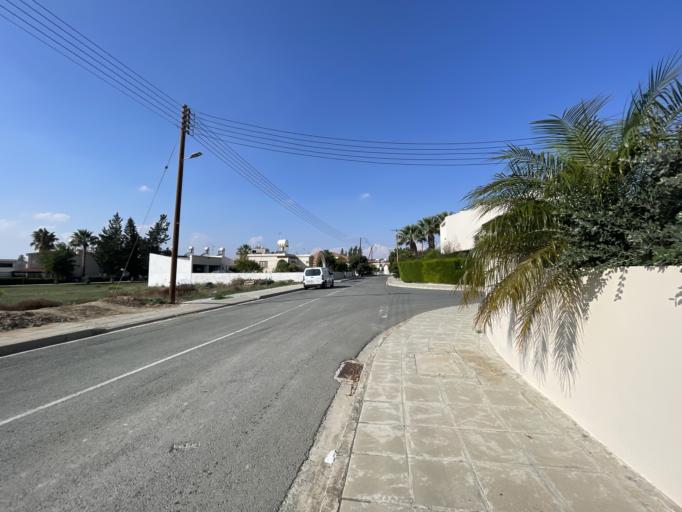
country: CY
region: Larnaka
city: Kiti
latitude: 34.8464
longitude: 33.5745
